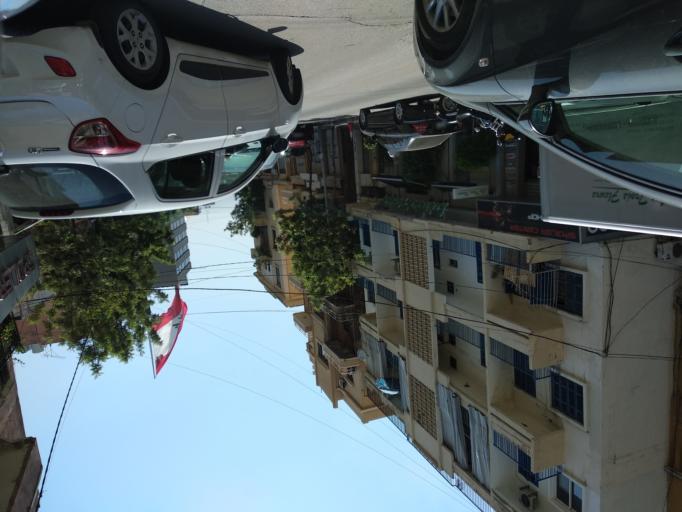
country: LB
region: Mont-Liban
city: Jdaidet el Matn
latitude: 33.8966
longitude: 35.5321
